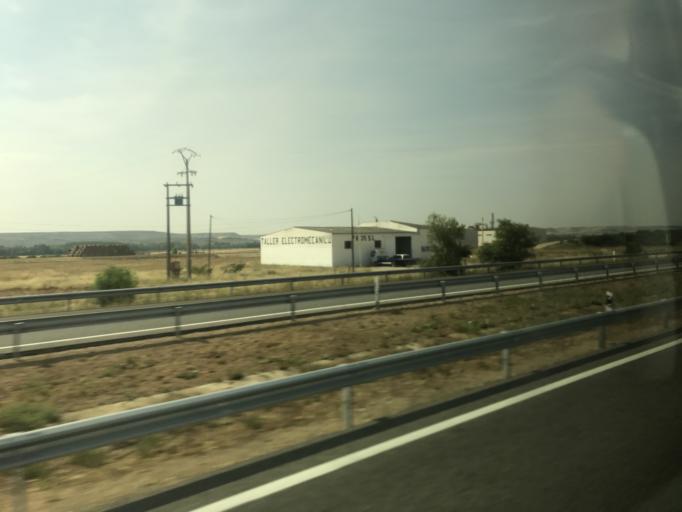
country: ES
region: Castille and Leon
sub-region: Provincia de Burgos
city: Villazopeque
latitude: 42.1997
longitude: -4.0228
